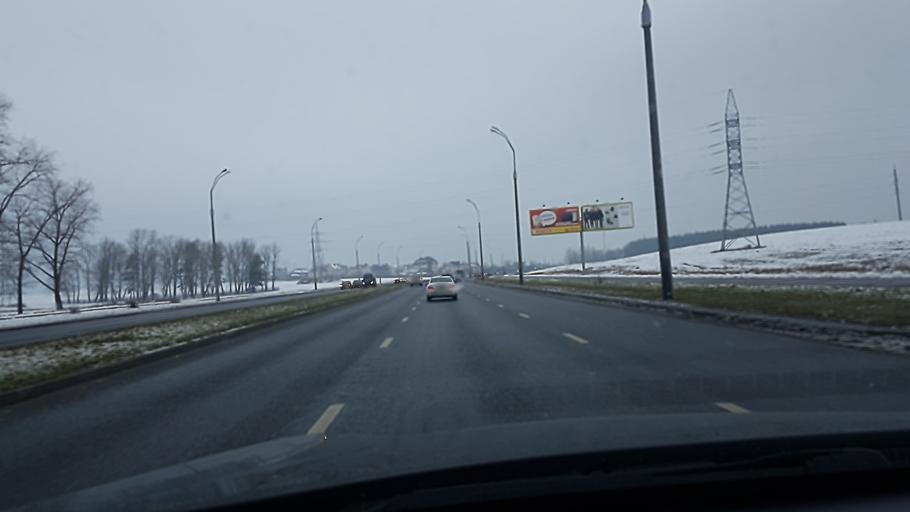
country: BY
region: Minsk
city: Minsk
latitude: 53.9469
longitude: 27.5378
